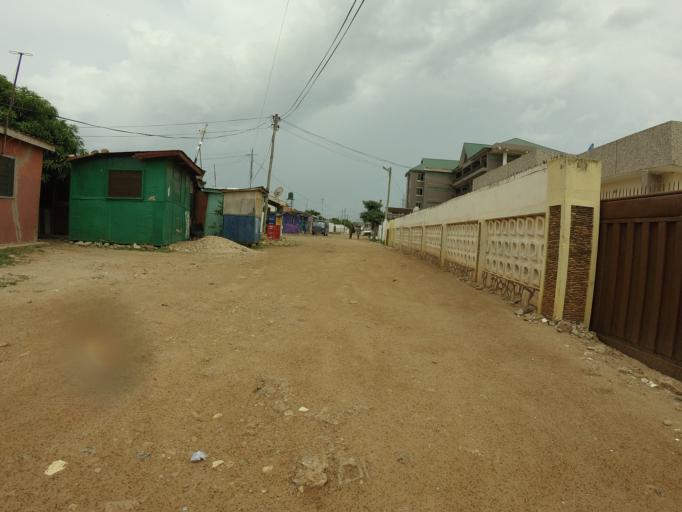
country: GH
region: Greater Accra
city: Accra
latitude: 5.6015
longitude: -0.2195
